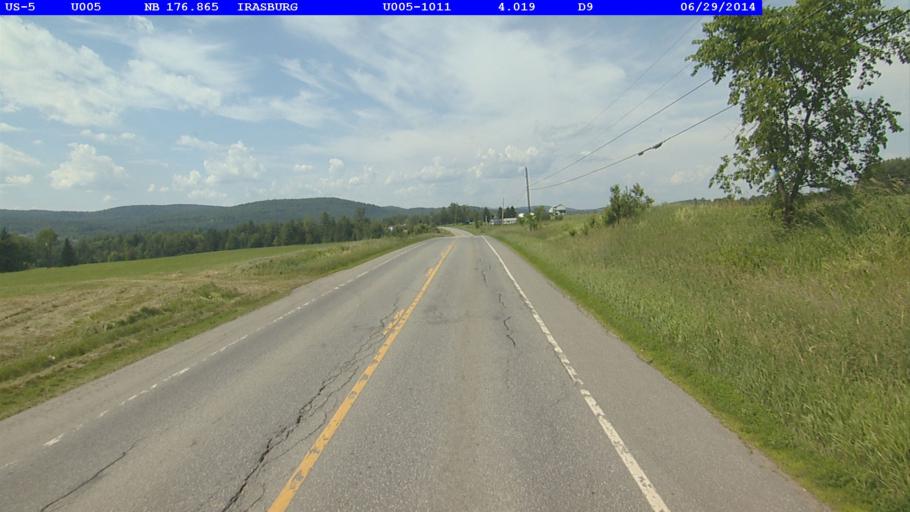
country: US
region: Vermont
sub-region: Orleans County
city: Newport
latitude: 44.8496
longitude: -72.2629
